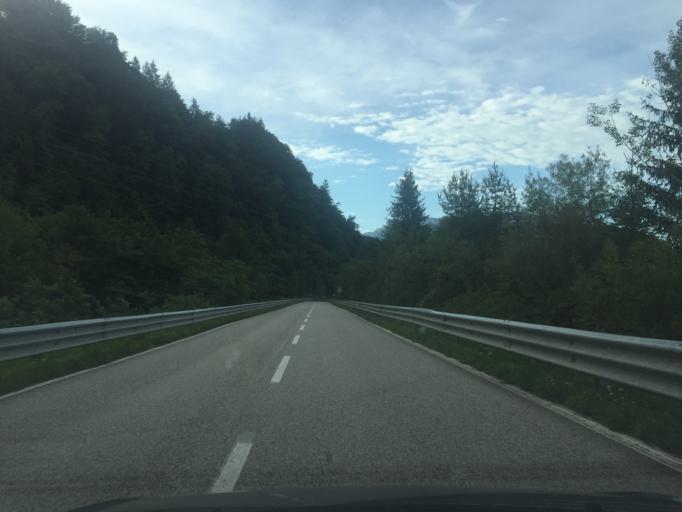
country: IT
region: Friuli Venezia Giulia
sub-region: Provincia di Udine
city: Raveo
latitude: 46.4535
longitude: 12.8761
